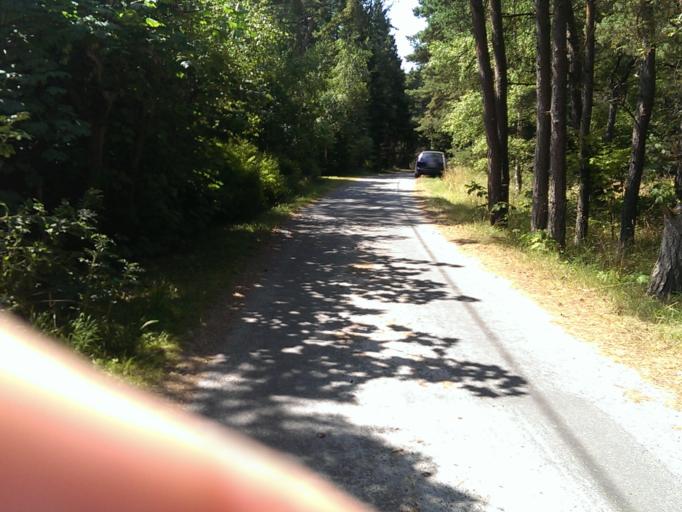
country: SE
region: Skane
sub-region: Simrishamns Kommun
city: Simrishamn
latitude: 55.4246
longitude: 14.2285
